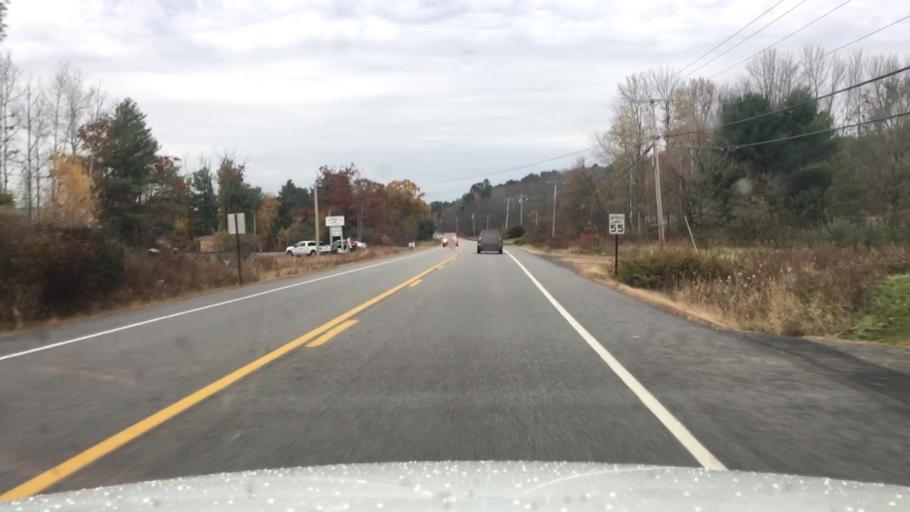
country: US
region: Maine
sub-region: Kennebec County
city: Pittston
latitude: 44.2128
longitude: -69.7554
